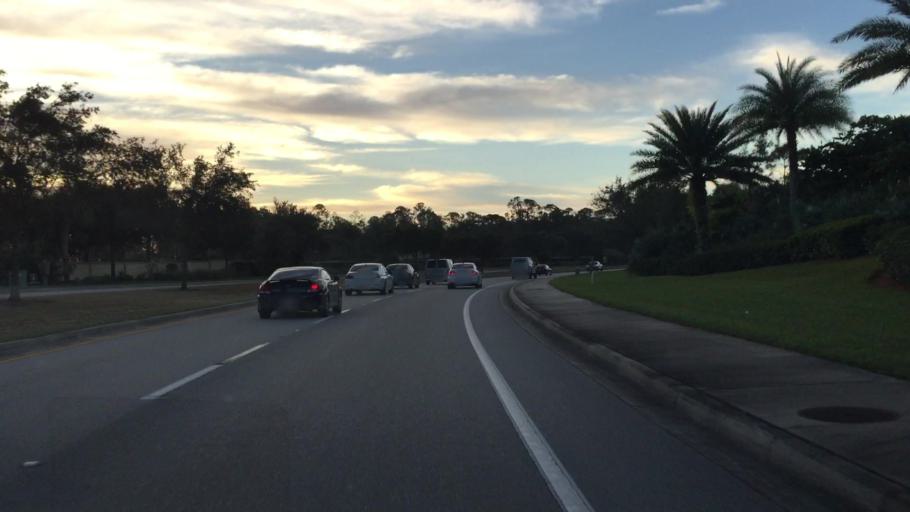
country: US
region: Florida
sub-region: Lee County
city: Gateway
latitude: 26.5793
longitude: -81.7794
